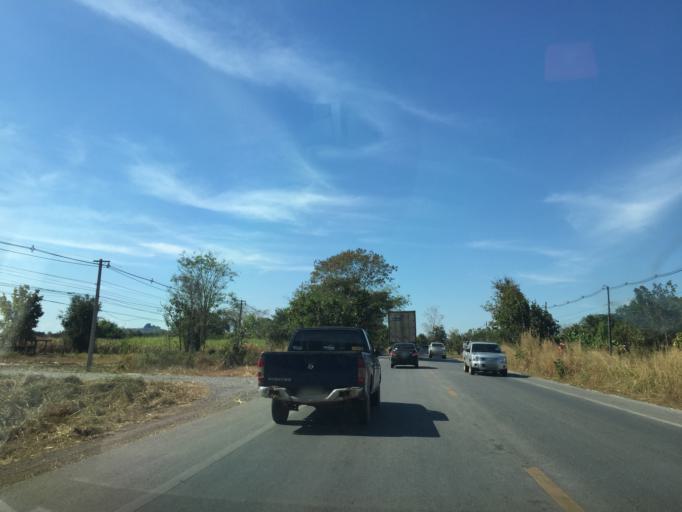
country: TH
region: Changwat Nong Bua Lamphu
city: Na Klang
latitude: 17.3159
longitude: 102.1612
